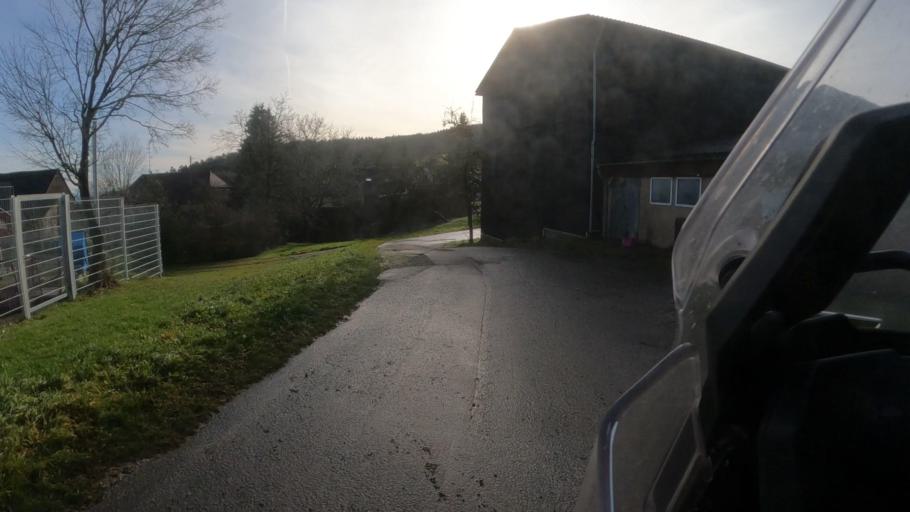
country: DE
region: Baden-Wuerttemberg
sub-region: Freiburg Region
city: Tengen
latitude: 47.7849
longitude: 8.6304
